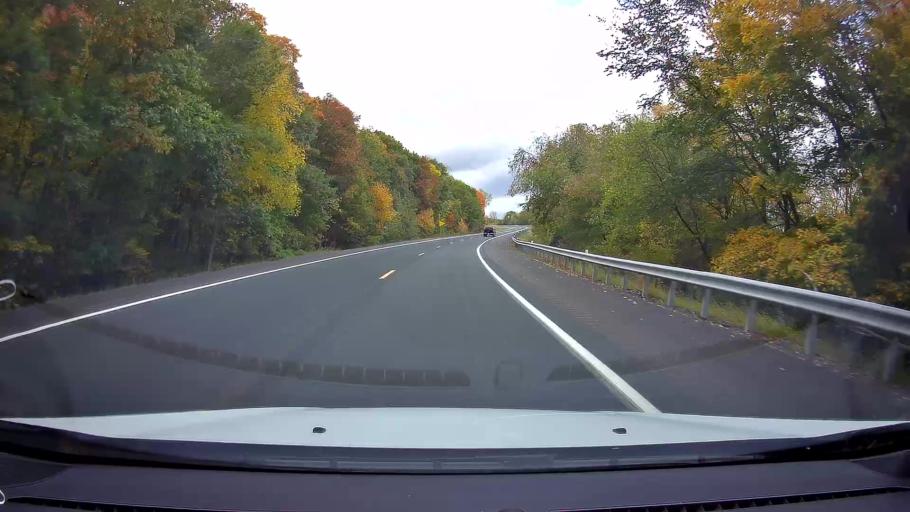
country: US
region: Wisconsin
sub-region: Polk County
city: Saint Croix Falls
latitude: 45.4127
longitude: -92.6541
